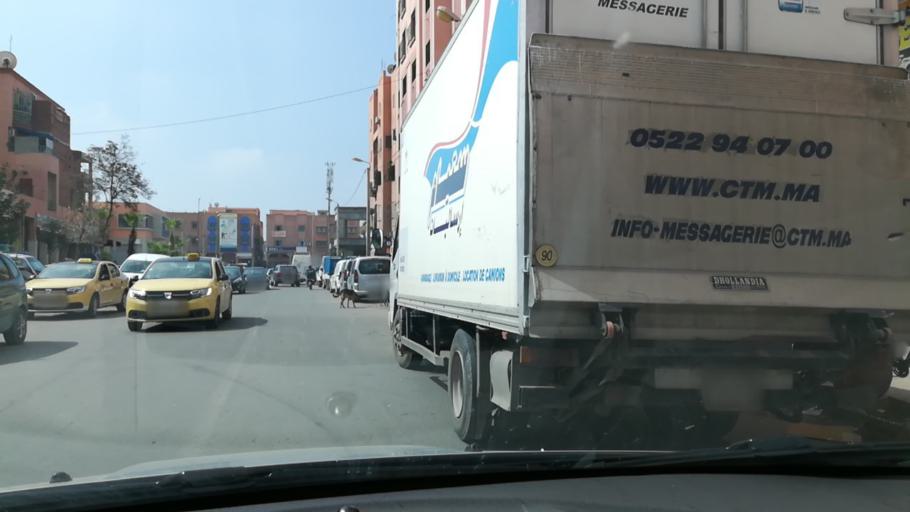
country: MA
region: Marrakech-Tensift-Al Haouz
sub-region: Marrakech
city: Marrakesh
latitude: 31.6292
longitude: -8.0625
